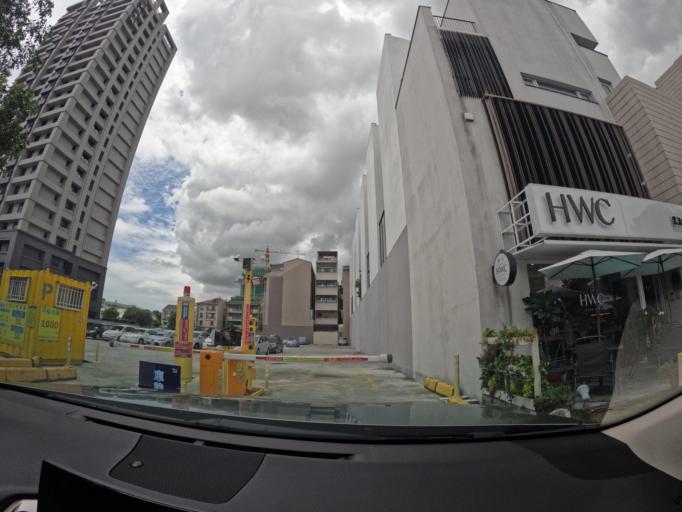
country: TW
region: Kaohsiung
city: Kaohsiung
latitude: 22.7267
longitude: 120.2955
